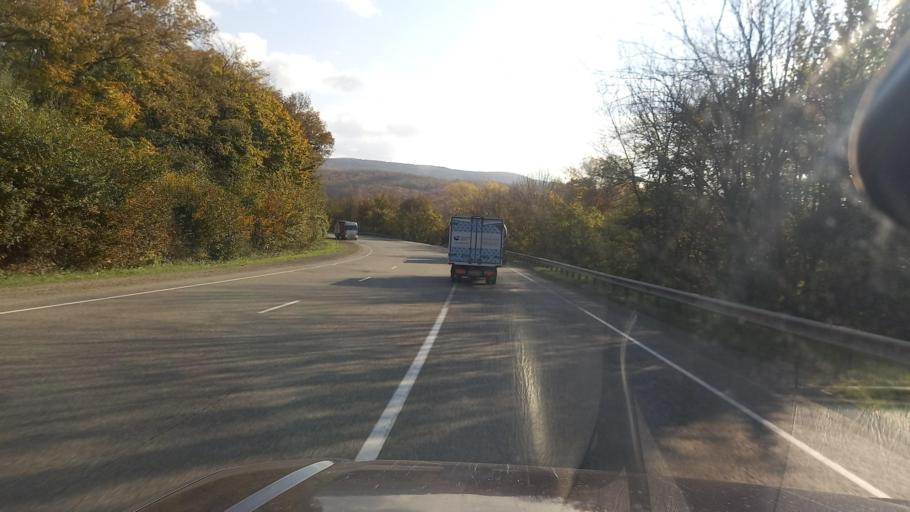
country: RU
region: Krasnodarskiy
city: Verkhnebakanskiy
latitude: 44.8412
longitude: 37.7063
